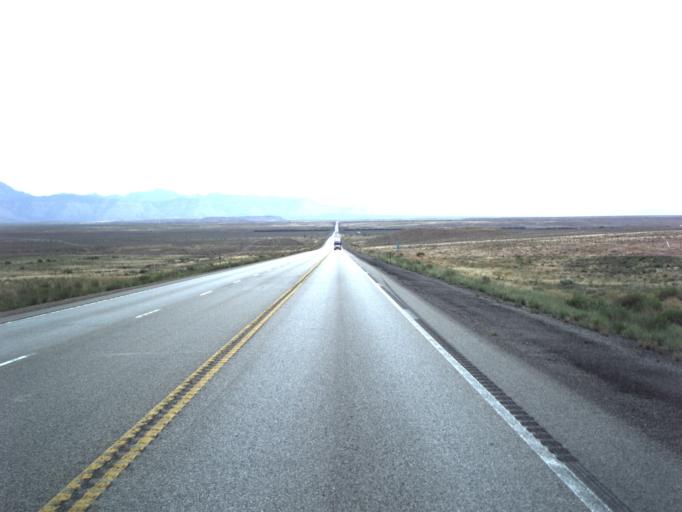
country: US
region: Utah
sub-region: Carbon County
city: Wellington
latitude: 39.5337
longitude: -110.5920
